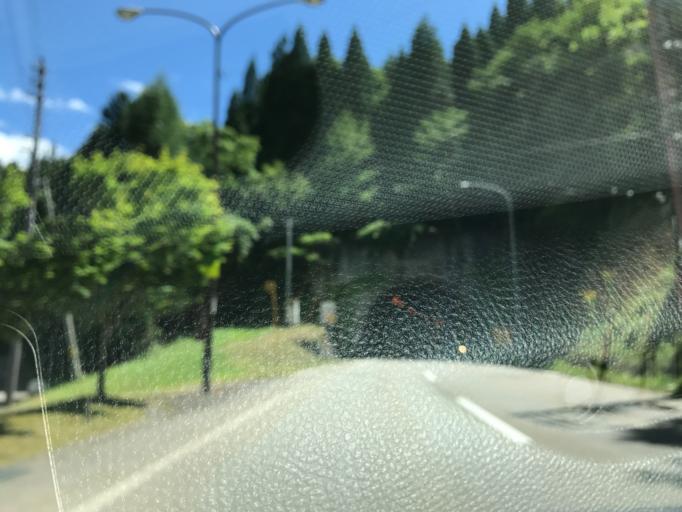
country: JP
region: Gifu
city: Takayama
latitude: 36.1033
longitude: 137.1179
